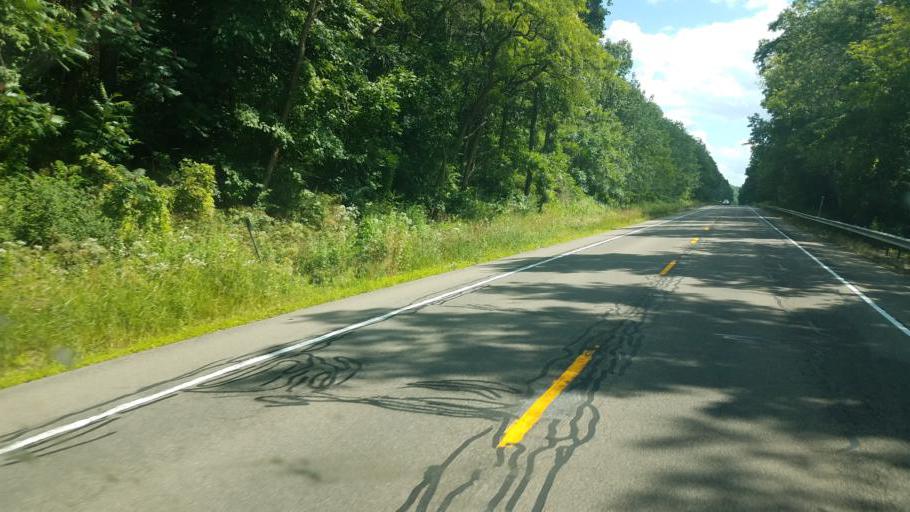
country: US
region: New York
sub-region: Steuben County
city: Sylvan Beach
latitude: 42.5368
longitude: -77.0993
